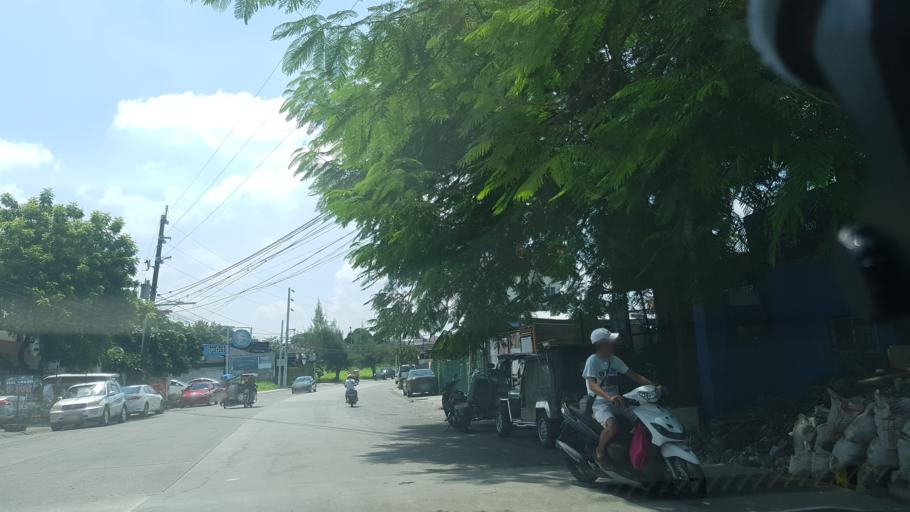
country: PH
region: Calabarzon
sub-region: Province of Rizal
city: Las Pinas
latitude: 14.4334
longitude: 120.9897
